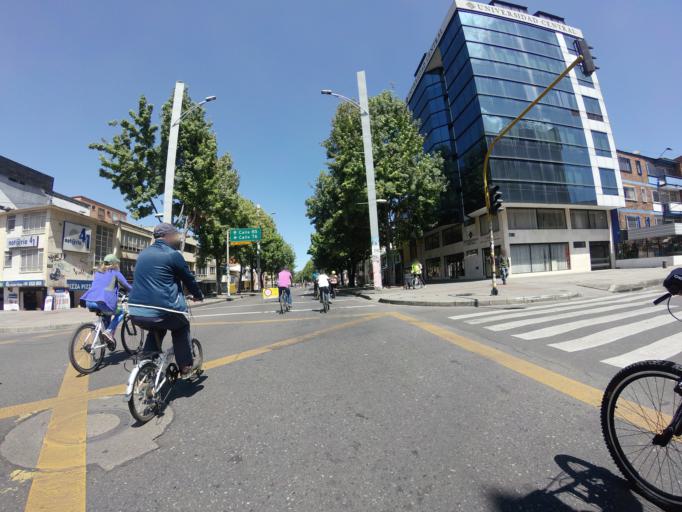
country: CO
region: Bogota D.C.
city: Barrio San Luis
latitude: 4.6620
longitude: -74.0597
